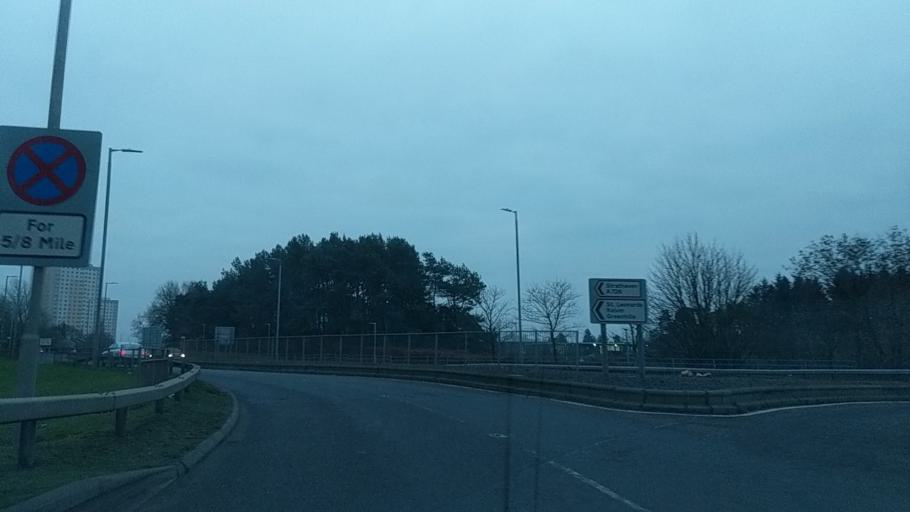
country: GB
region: Scotland
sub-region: South Lanarkshire
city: East Kilbride
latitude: 55.7579
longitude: -4.1654
